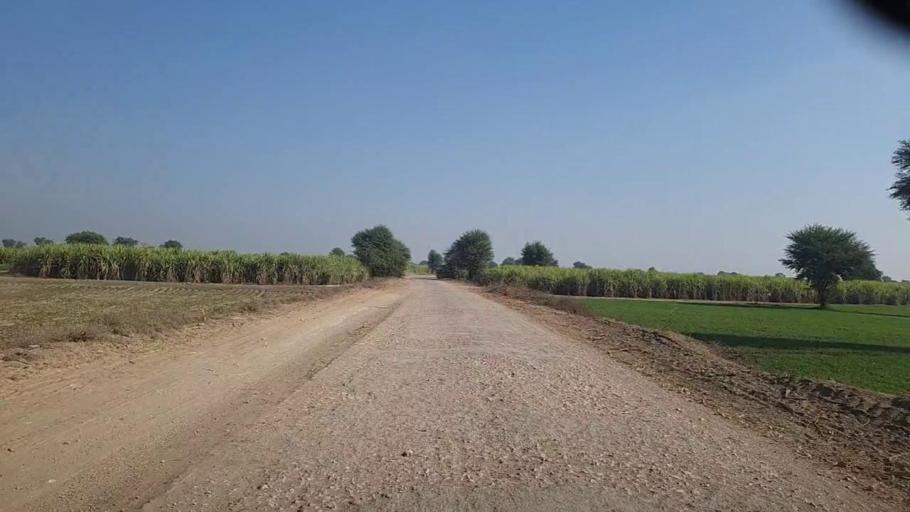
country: PK
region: Sindh
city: Darya Khan Marri
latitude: 26.6701
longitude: 68.3295
